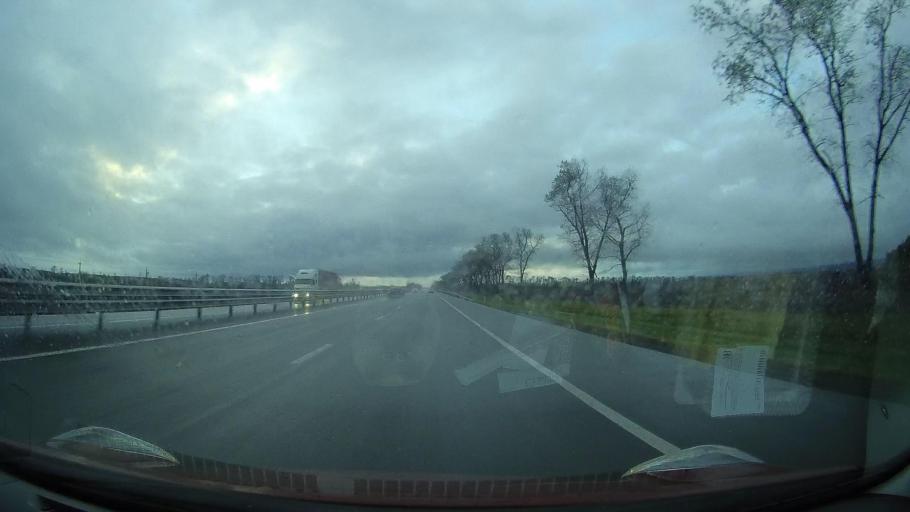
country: RU
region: Stavropol'skiy
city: Zavetnoye
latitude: 44.7882
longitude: 41.5068
